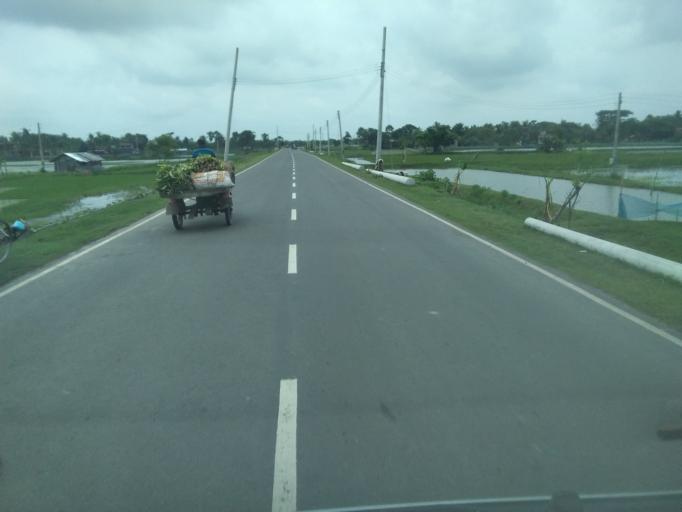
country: BD
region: Khulna
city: Satkhira
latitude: 22.7061
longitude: 89.0561
